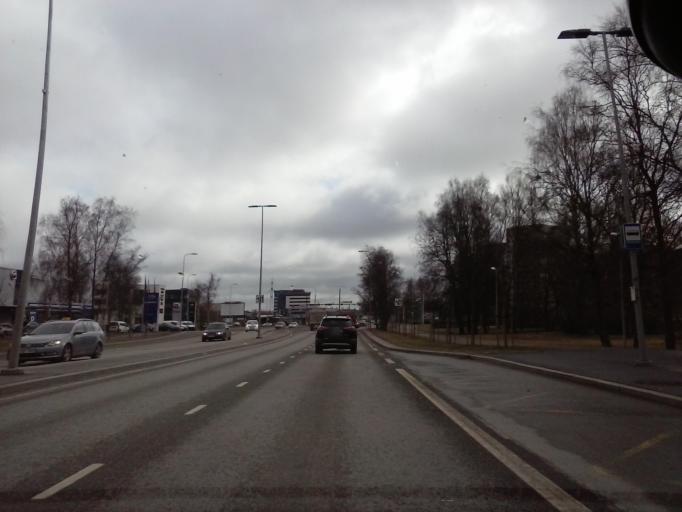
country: EE
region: Harju
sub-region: Saue vald
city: Laagri
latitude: 59.4174
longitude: 24.6545
